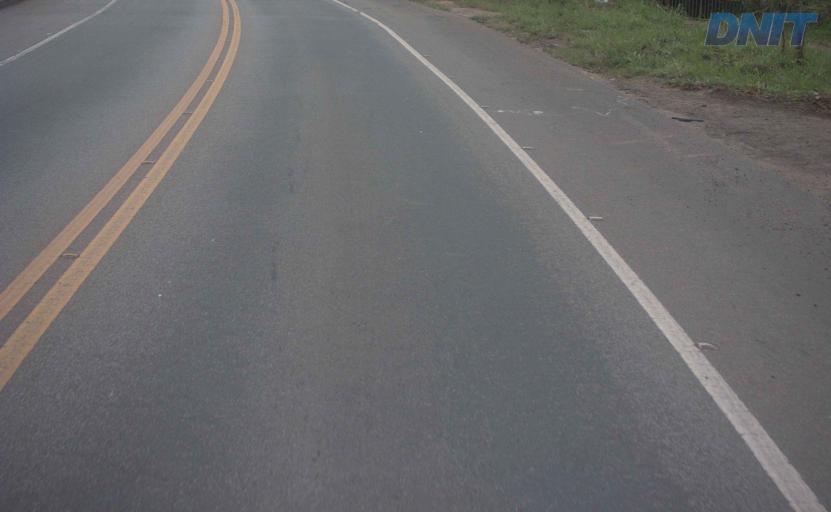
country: BR
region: Minas Gerais
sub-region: Coronel Fabriciano
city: Coronel Fabriciano
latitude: -19.5203
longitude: -42.5811
